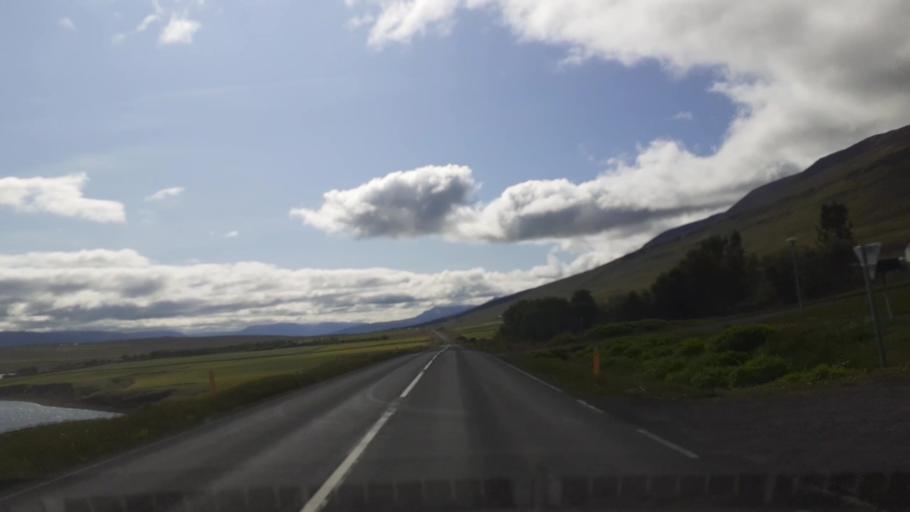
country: IS
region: Northeast
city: Akureyri
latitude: 65.8703
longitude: -18.2631
